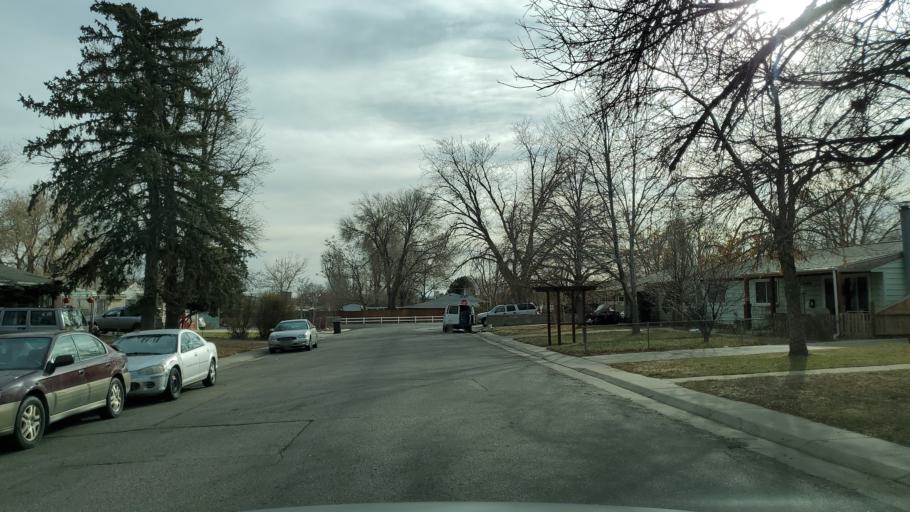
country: US
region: Colorado
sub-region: Adams County
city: Twin Lakes
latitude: 39.8282
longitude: -105.0193
